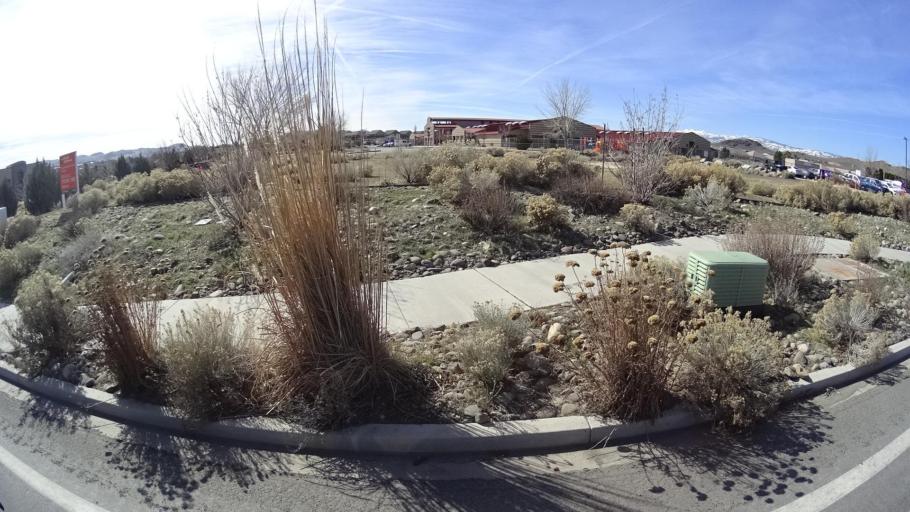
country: US
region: Nevada
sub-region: Washoe County
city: Sun Valley
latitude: 39.5852
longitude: -119.7322
